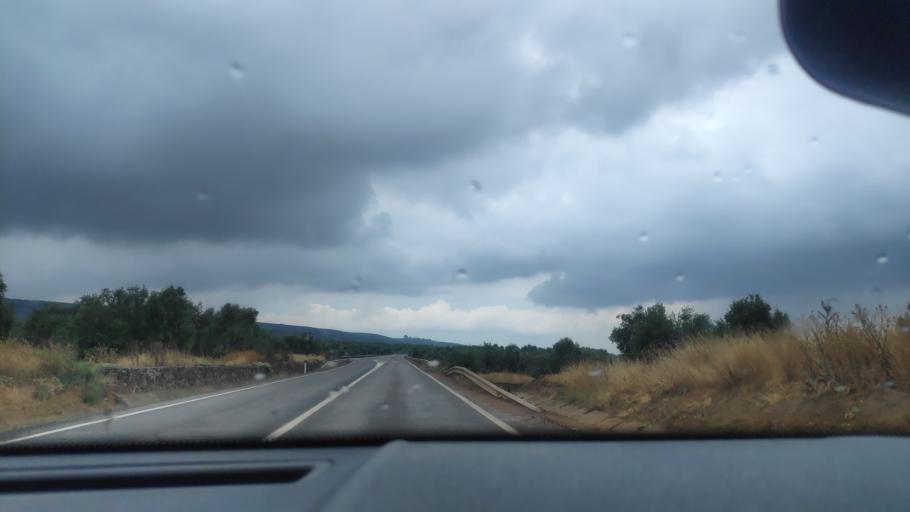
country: ES
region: Andalusia
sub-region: Provincia de Jaen
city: Jabalquinto
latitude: 38.0436
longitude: -3.7329
